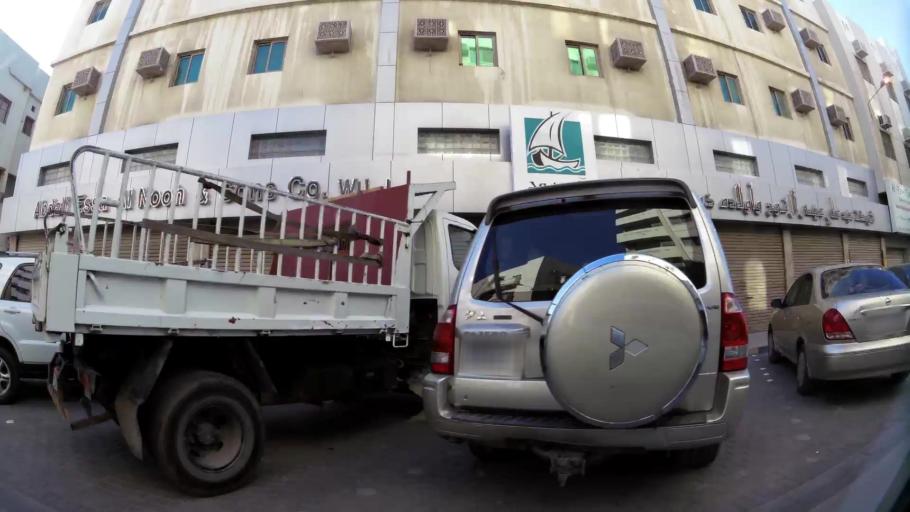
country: BH
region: Manama
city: Manama
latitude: 26.2260
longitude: 50.5720
